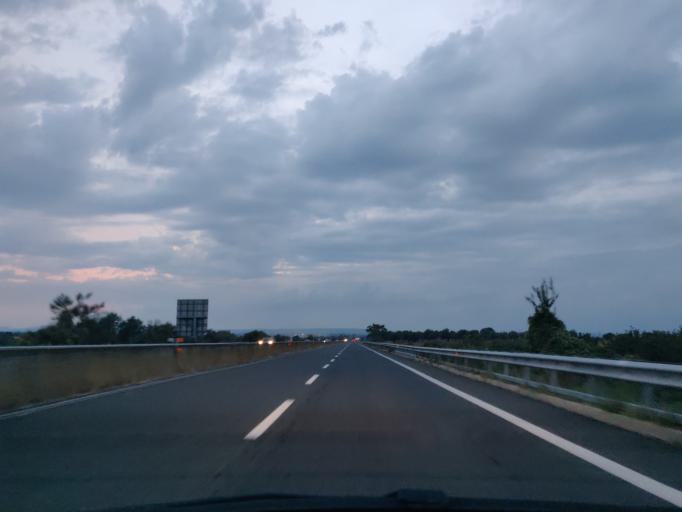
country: IT
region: Latium
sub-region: Provincia di Viterbo
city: Vetralla
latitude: 42.3706
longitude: 12.0405
